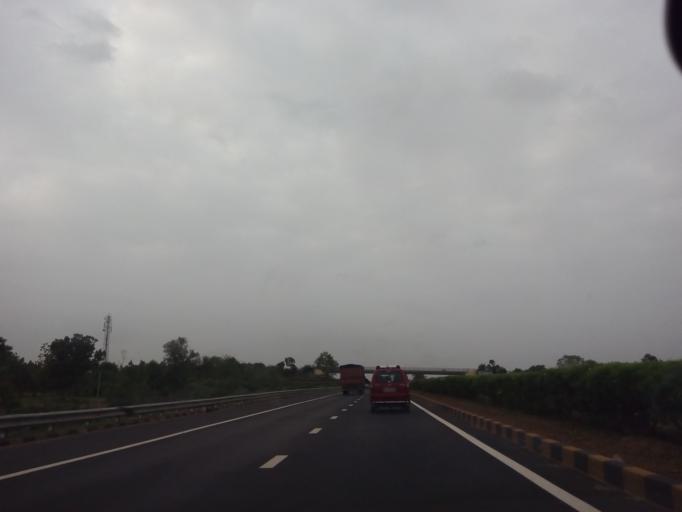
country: IN
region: Gujarat
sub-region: Kheda
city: Mahemdavad
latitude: 22.7931
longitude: 72.8417
